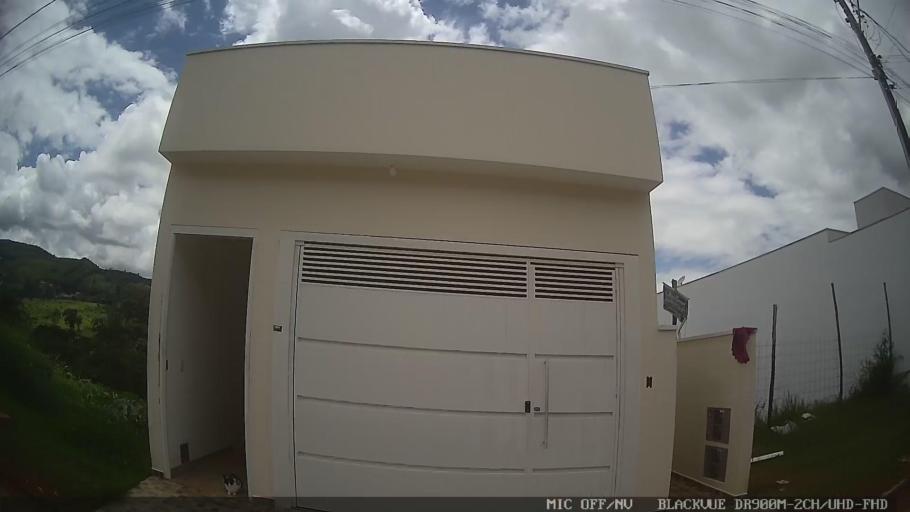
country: BR
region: Minas Gerais
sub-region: Extrema
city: Extrema
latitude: -22.7962
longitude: -46.4427
